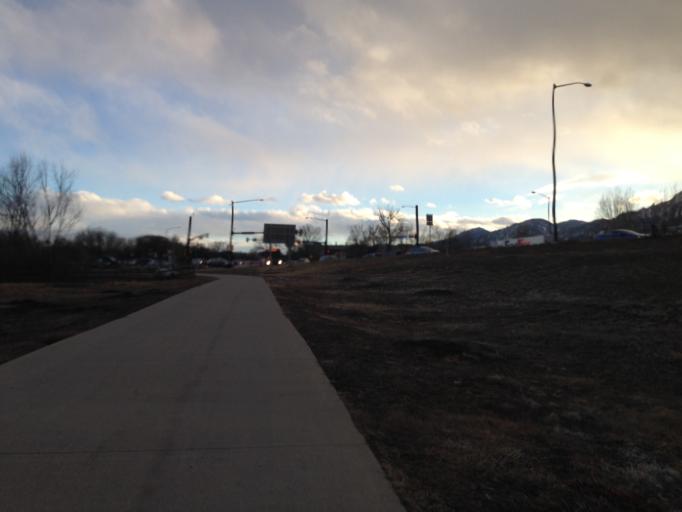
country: US
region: Colorado
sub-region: Boulder County
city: Boulder
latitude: 40.0159
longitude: -105.2408
